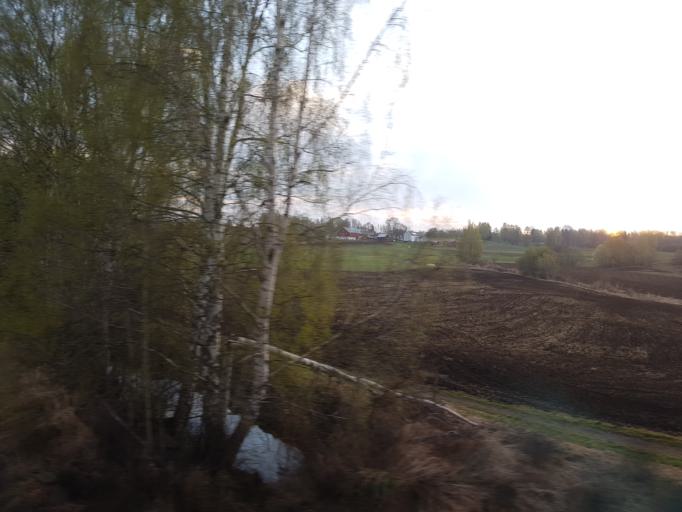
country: NO
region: Hedmark
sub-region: Hamar
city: Hamar
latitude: 60.7530
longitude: 11.1232
